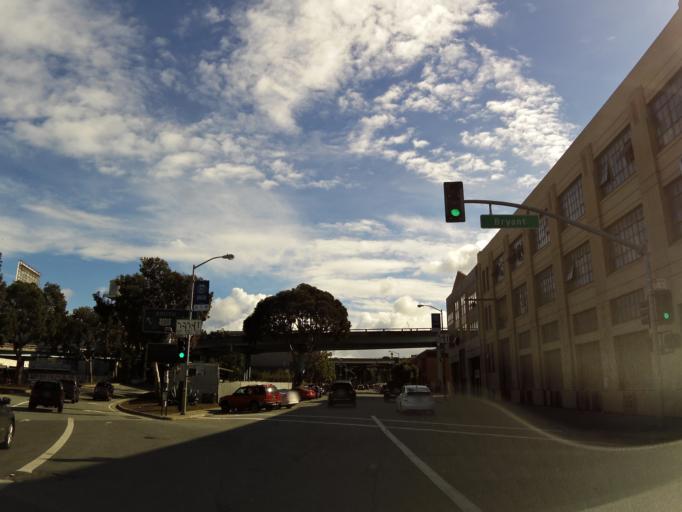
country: US
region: California
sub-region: San Francisco County
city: San Francisco
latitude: 37.7705
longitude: -122.4099
